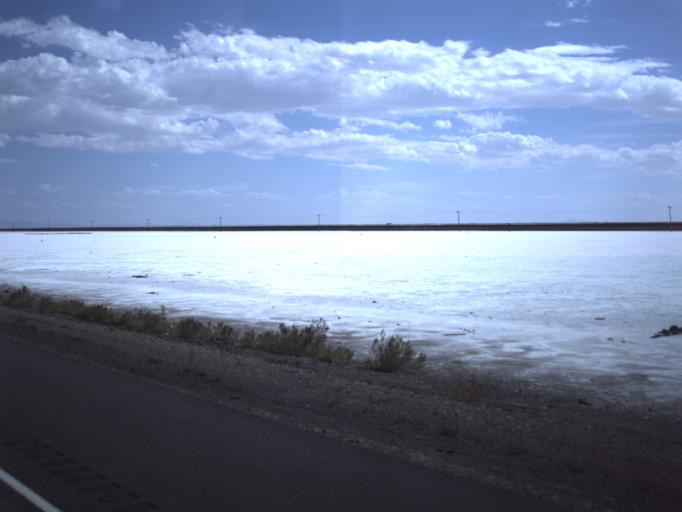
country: US
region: Utah
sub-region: Tooele County
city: Wendover
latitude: 40.7388
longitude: -113.8689
